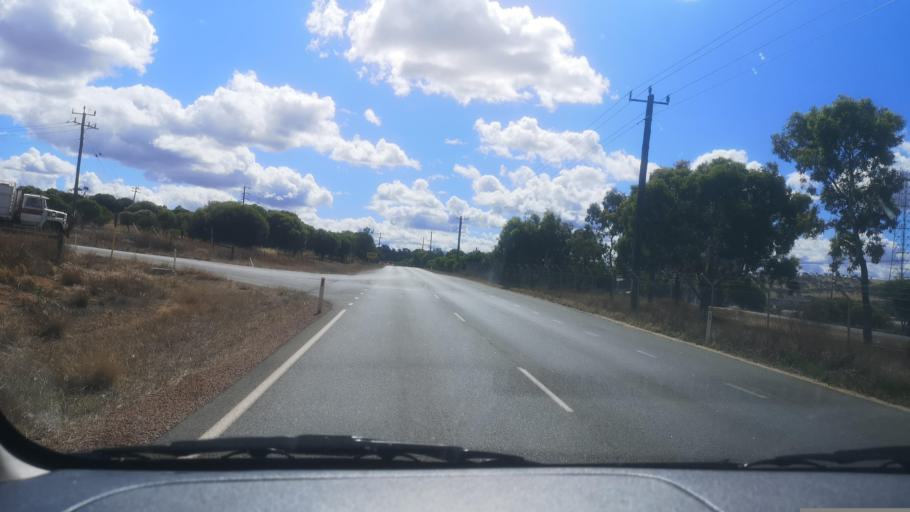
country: AU
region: Western Australia
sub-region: Northam
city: Northam
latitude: -31.6426
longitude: 116.6317
